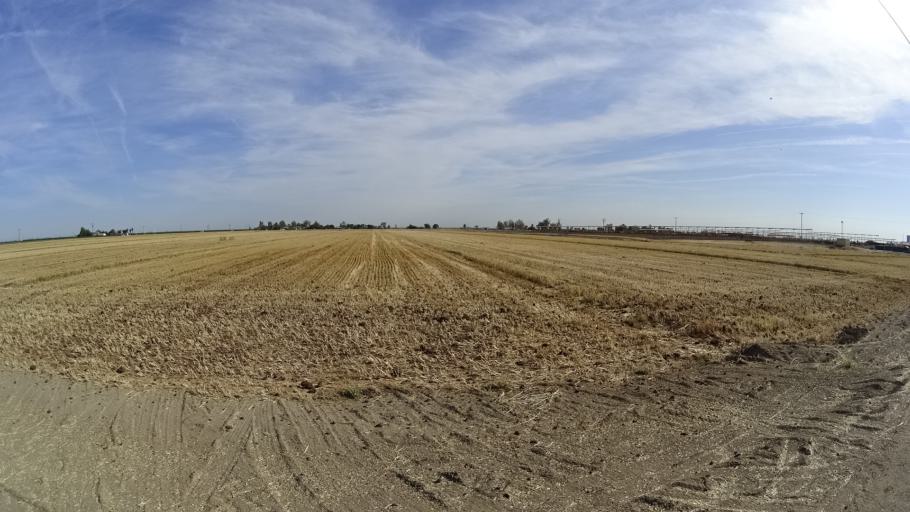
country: US
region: California
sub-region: Tulare County
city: Goshen
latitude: 36.3417
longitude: -119.4729
